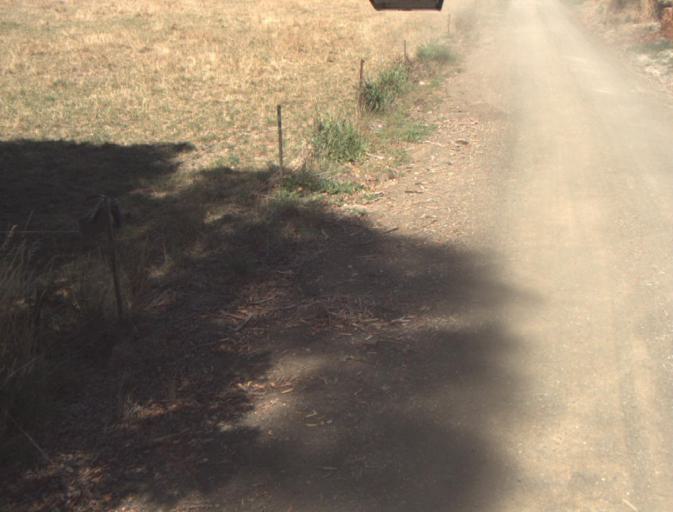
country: AU
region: Tasmania
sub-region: Launceston
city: Mayfield
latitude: -41.2635
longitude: 147.1494
